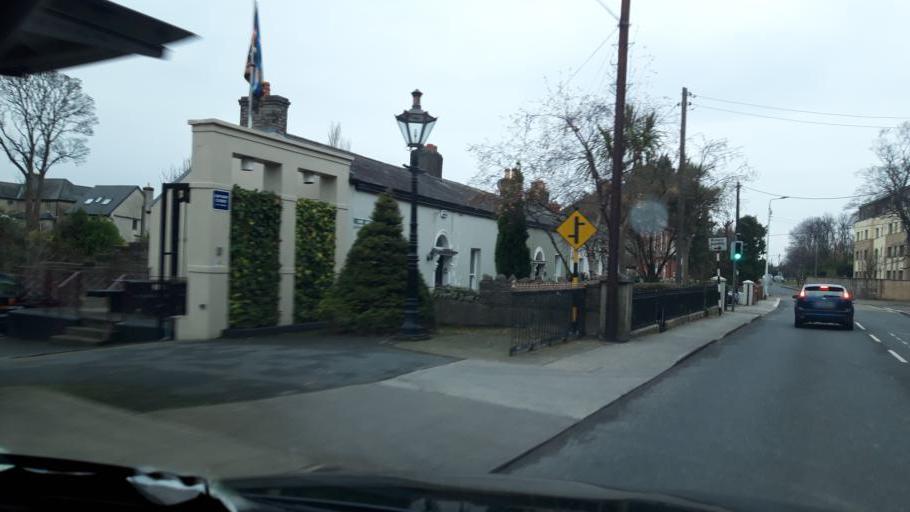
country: IE
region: Leinster
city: Dundrum
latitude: 53.2953
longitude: -6.2462
